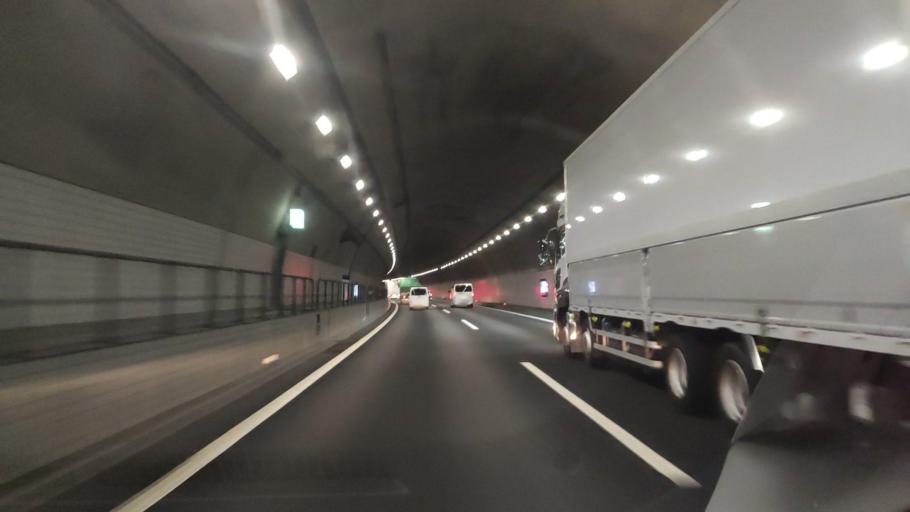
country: JP
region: Tokyo
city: Hachioji
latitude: 35.6034
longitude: 139.2672
